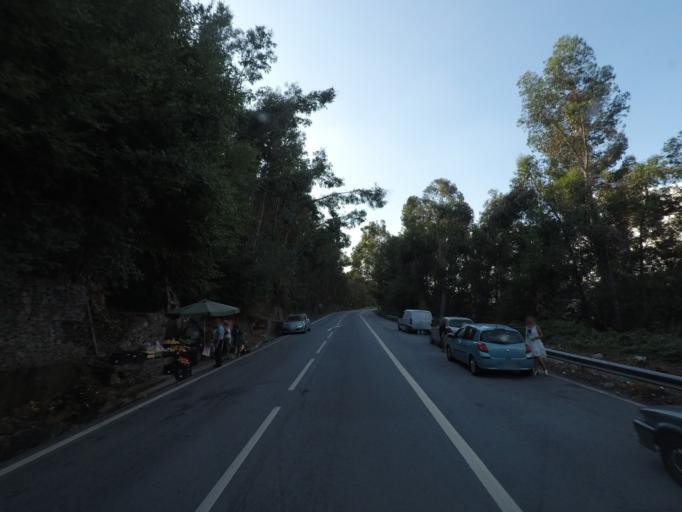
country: PT
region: Vila Real
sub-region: Mesao Frio
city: Mesao Frio
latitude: 41.1741
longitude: -7.9210
